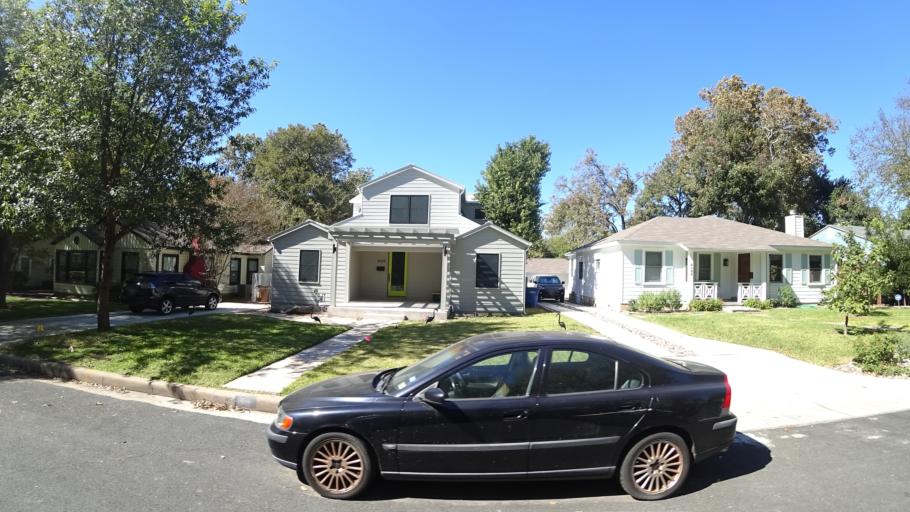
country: US
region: Texas
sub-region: Travis County
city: Austin
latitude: 30.3125
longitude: -97.7470
